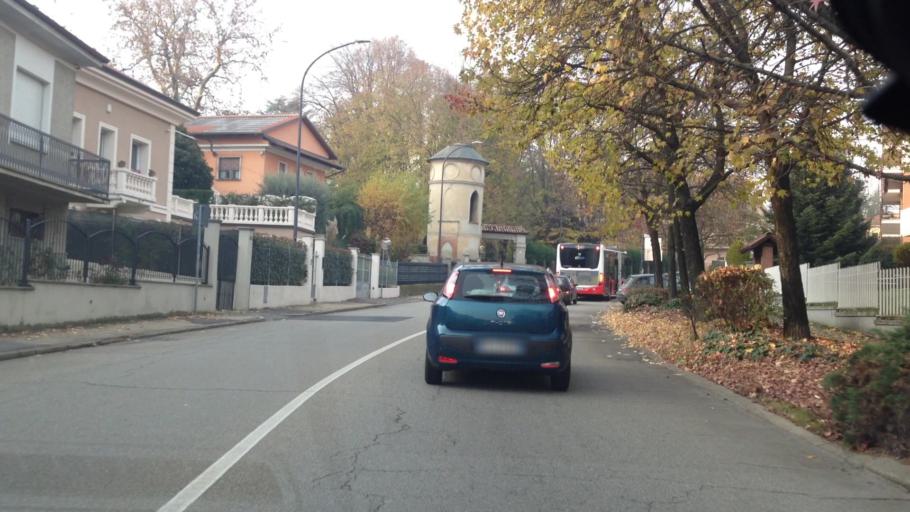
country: IT
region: Piedmont
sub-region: Provincia di Asti
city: Asti
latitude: 44.9062
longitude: 8.2076
